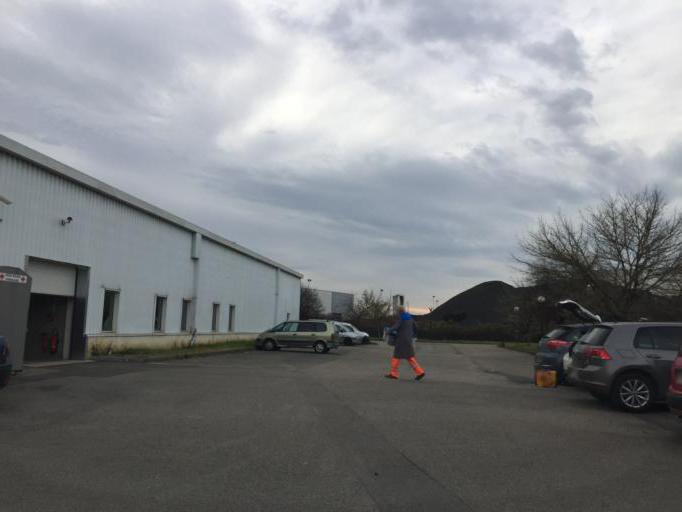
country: FR
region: Rhone-Alpes
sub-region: Departement de l'Ain
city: Jassans-Riottier
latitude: 45.9826
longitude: 4.7451
